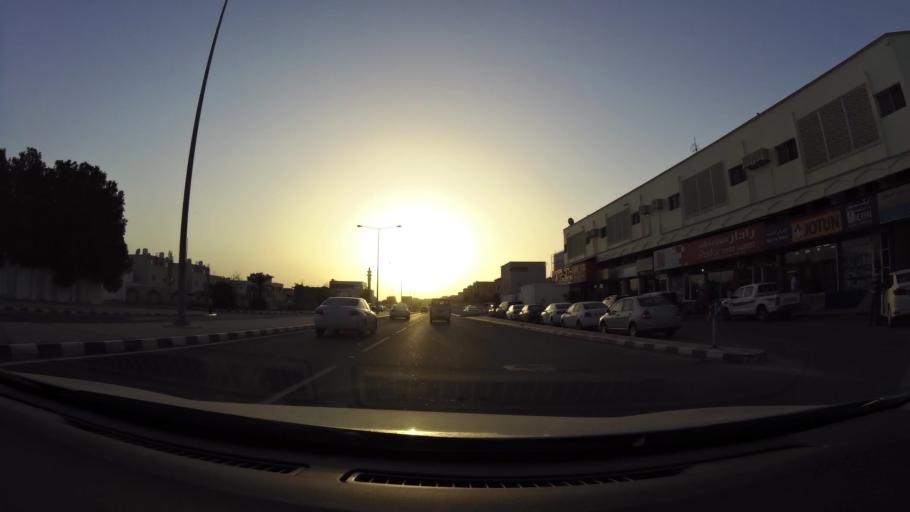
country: QA
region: Baladiyat ar Rayyan
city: Ar Rayyan
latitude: 25.3133
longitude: 51.4671
